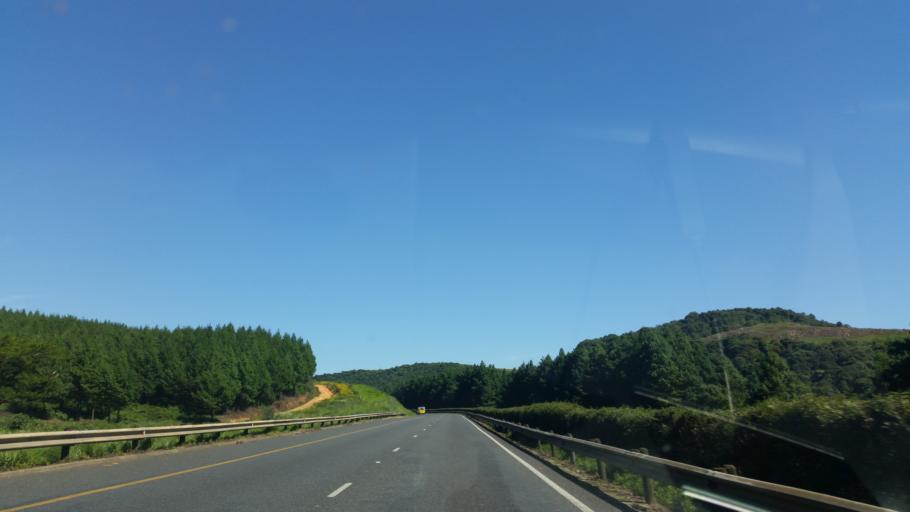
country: ZA
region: KwaZulu-Natal
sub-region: uMgungundlovu District Municipality
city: Mooirivier
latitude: -29.3458
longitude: 30.0838
